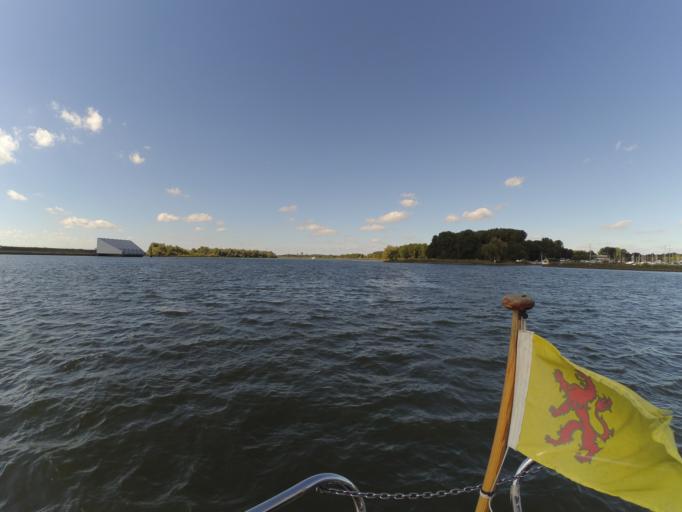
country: NL
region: South Holland
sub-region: Gemeente Albrandswaard
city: Rhoon
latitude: 51.8405
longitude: 4.4253
